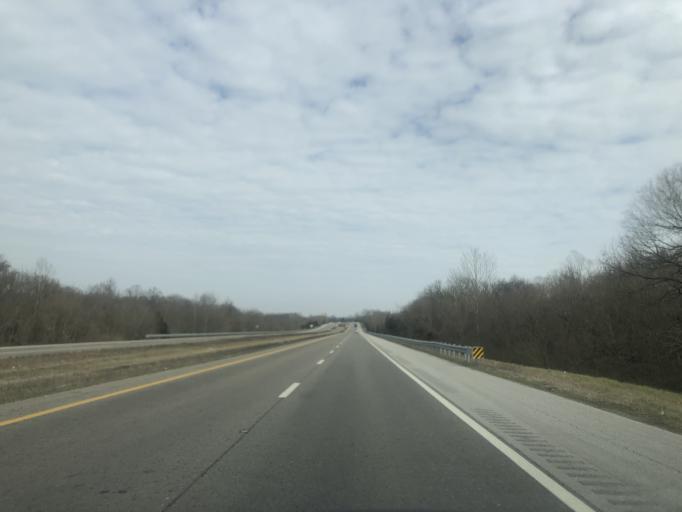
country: US
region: Tennessee
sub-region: Maury County
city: Mount Pleasant
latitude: 35.5860
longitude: -87.1329
